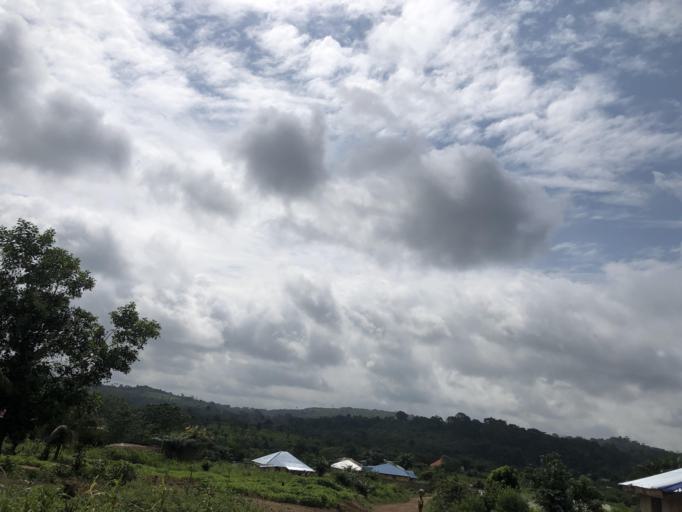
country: SL
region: Eastern Province
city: Kailahun
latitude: 8.2886
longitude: -10.5577
